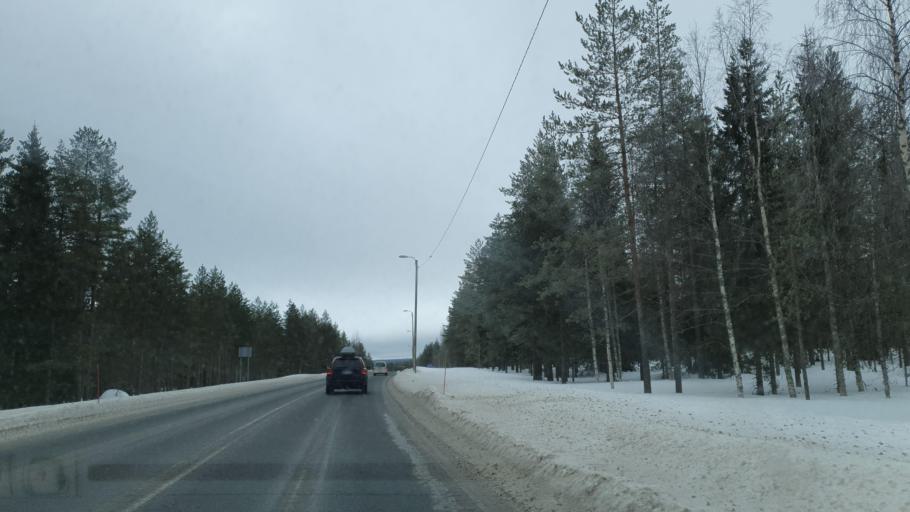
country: FI
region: Lapland
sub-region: Torniolaakso
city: Ylitornio
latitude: 66.2096
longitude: 23.7976
